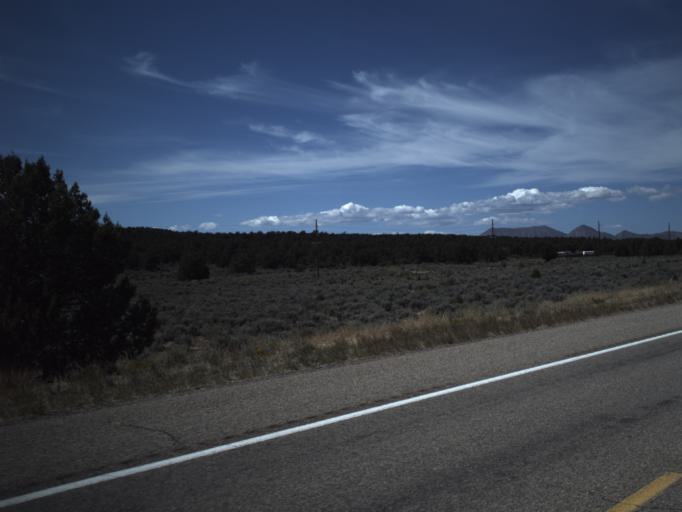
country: US
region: Utah
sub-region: Washington County
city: Ivins
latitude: 37.2770
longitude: -113.6496
